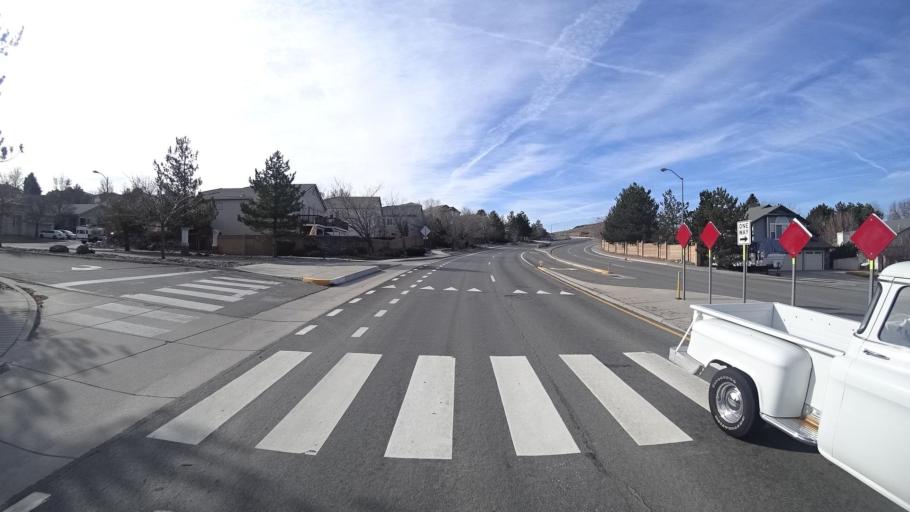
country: US
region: Nevada
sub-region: Washoe County
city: Sparks
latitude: 39.5747
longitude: -119.7192
